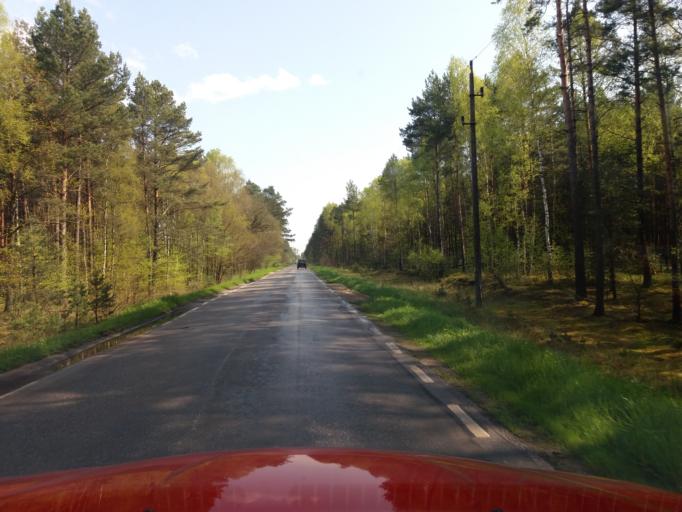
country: PL
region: West Pomeranian Voivodeship
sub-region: Powiat drawski
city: Kalisz Pomorski
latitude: 53.2690
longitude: 15.8693
